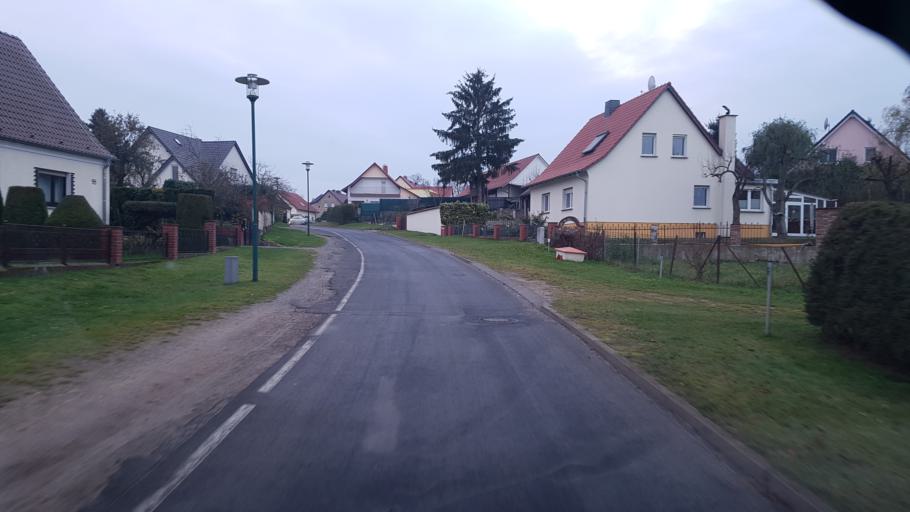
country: DE
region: Brandenburg
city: Wiesenau
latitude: 52.1855
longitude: 14.5799
